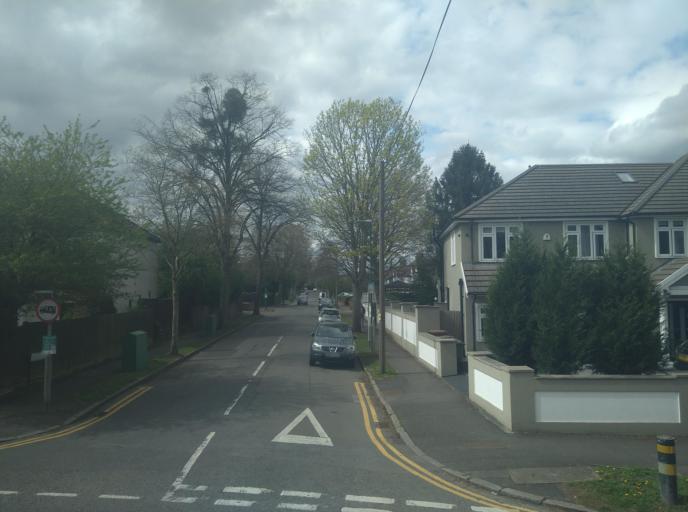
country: GB
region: England
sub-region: Greater London
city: Purley
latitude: 51.3532
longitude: -0.1376
